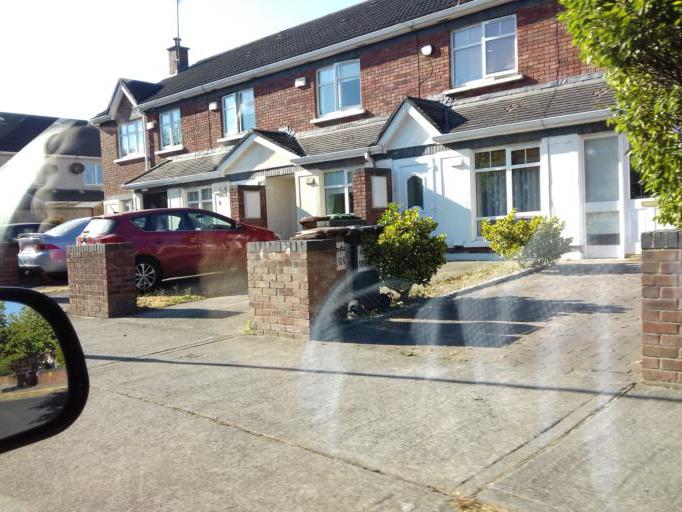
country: IE
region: Leinster
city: Hartstown
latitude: 53.3908
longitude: -6.4286
